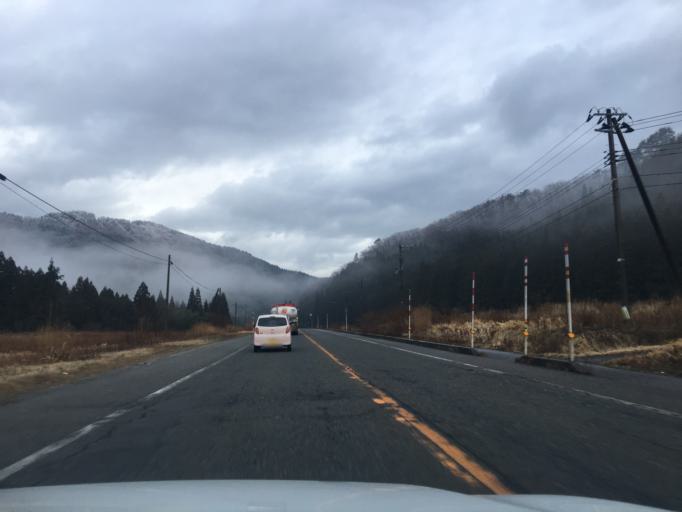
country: JP
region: Niigata
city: Murakami
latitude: 38.4470
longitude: 139.5807
